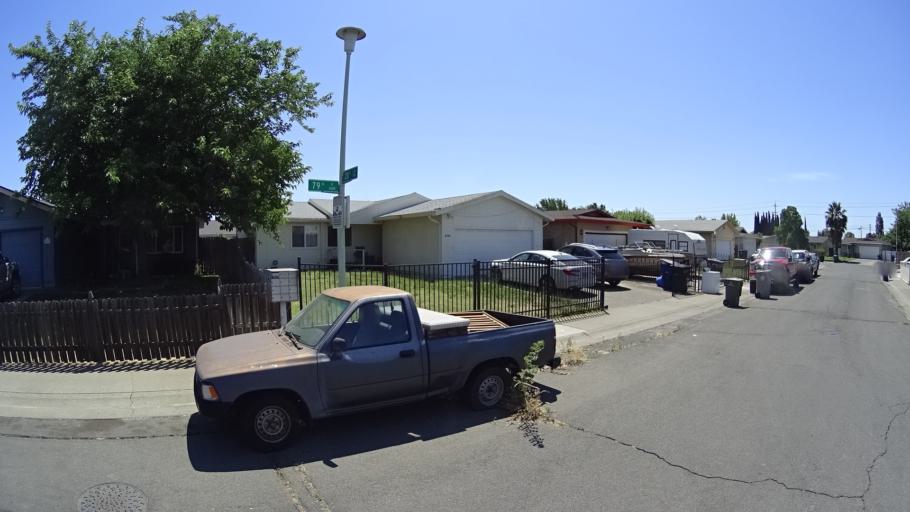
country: US
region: California
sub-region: Sacramento County
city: Florin
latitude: 38.5330
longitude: -121.4123
